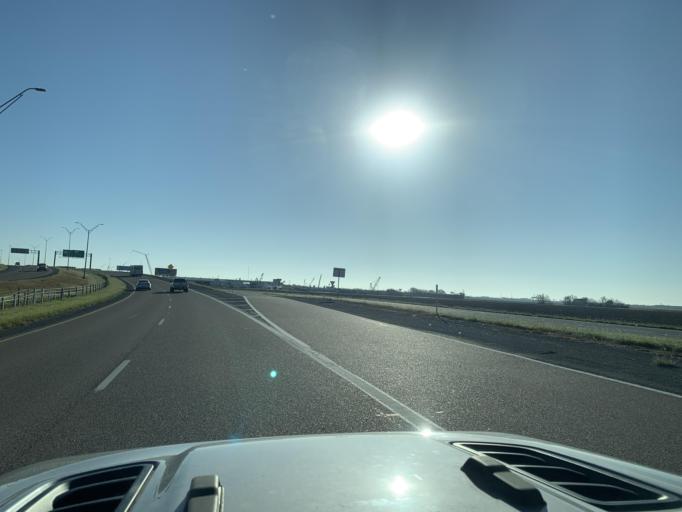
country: US
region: Texas
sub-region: Nueces County
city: Corpus Christi
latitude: 27.7820
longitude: -97.4815
